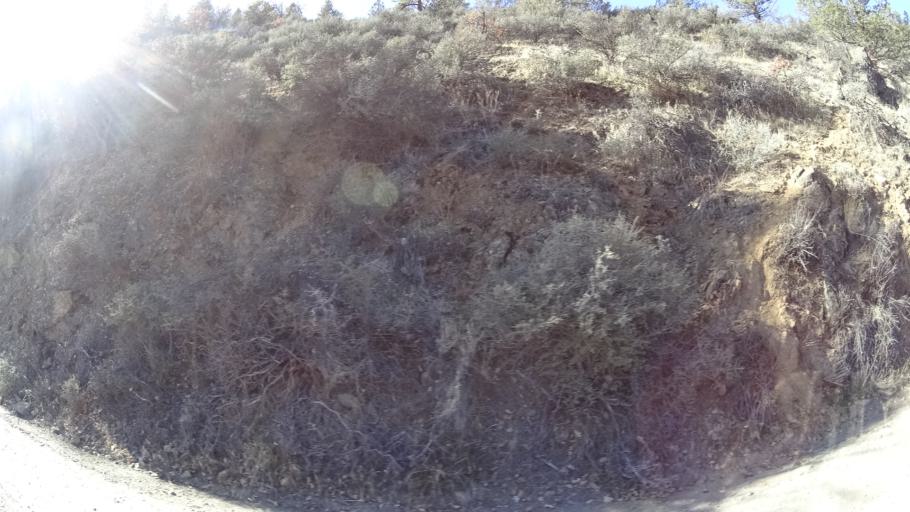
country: US
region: California
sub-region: Siskiyou County
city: Yreka
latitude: 41.7925
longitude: -122.6112
